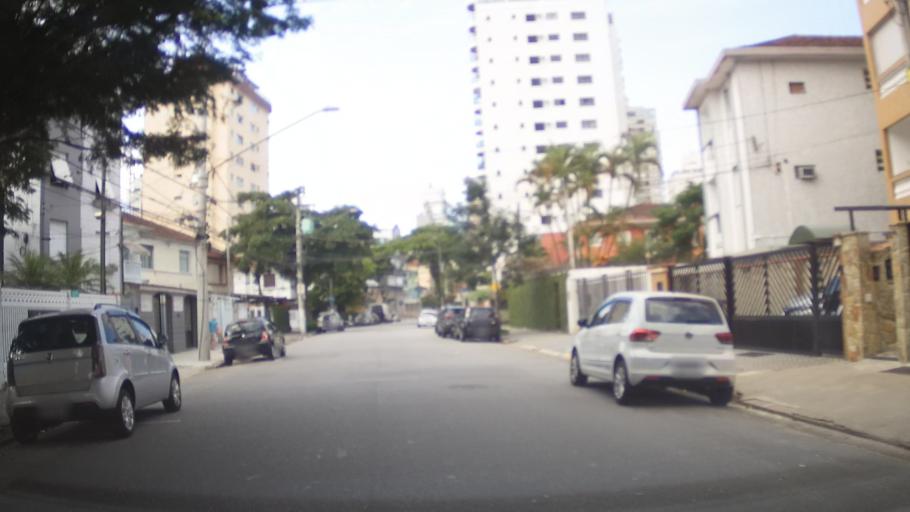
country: BR
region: Sao Paulo
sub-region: Santos
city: Santos
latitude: -23.9599
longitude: -46.3264
